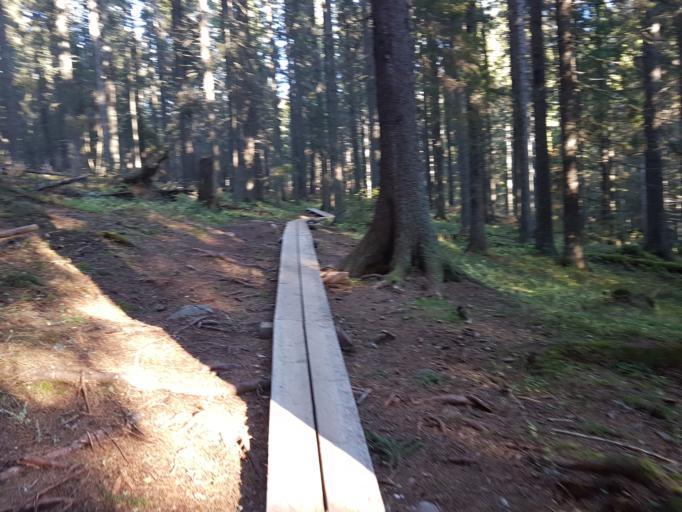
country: SE
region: Vaesternorrland
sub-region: OErnskoeldsviks Kommun
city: Kopmanholmen
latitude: 63.0902
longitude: 18.4958
